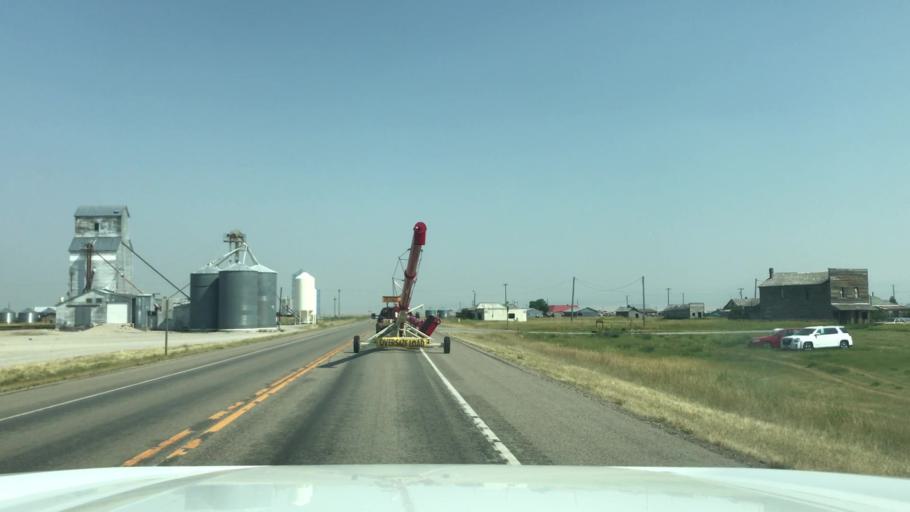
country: US
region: Montana
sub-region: Judith Basin County
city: Stanford
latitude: 47.0546
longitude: -109.9117
